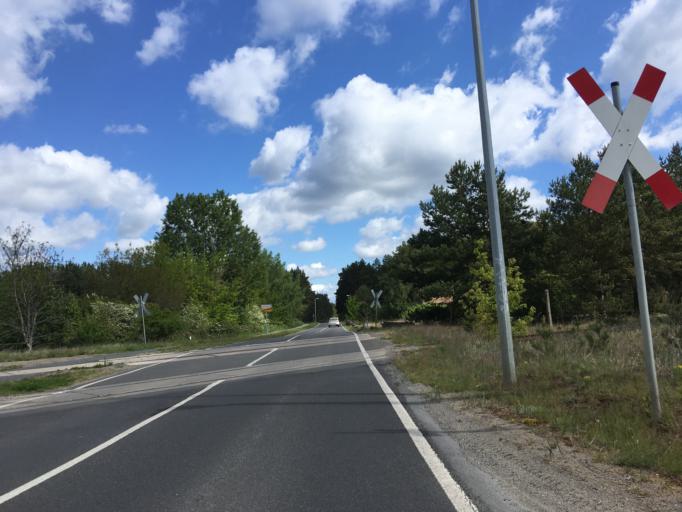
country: DE
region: Brandenburg
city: Oranienburg
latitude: 52.7786
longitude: 13.2588
